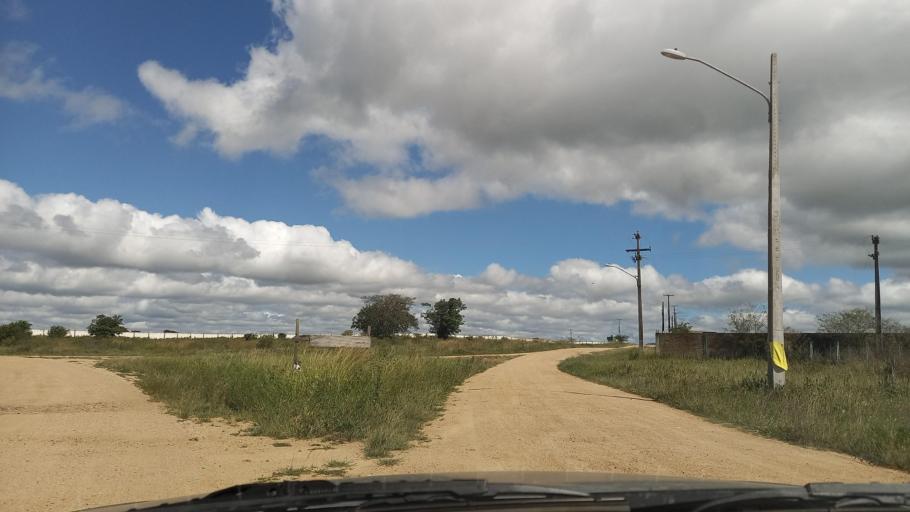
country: BR
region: Pernambuco
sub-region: Caruaru
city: Caruaru
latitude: -8.2325
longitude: -35.9820
